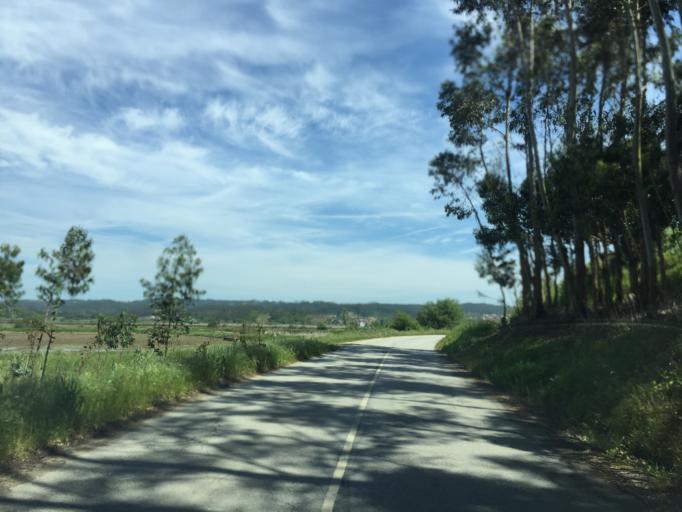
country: PT
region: Leiria
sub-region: Pombal
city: Lourical
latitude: 40.0692
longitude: -8.7495
